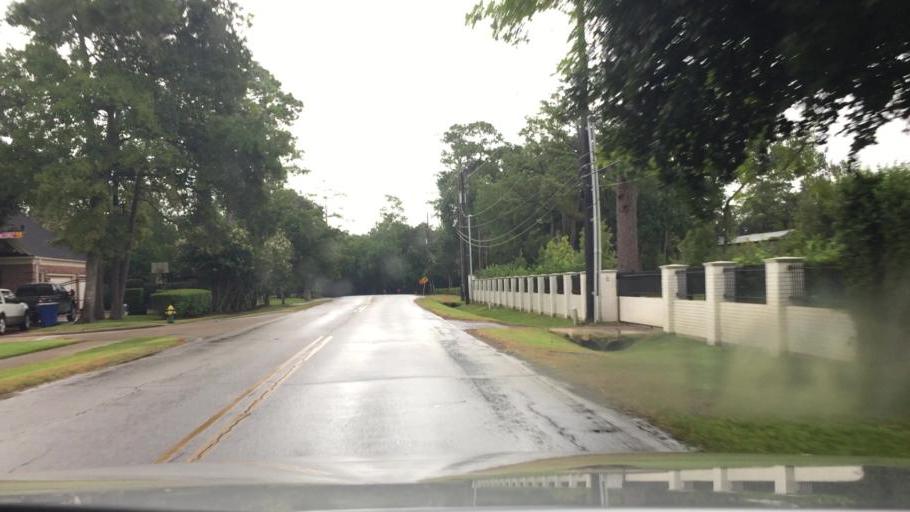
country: US
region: Texas
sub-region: Harris County
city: Hedwig Village
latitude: 29.7734
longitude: -95.5194
